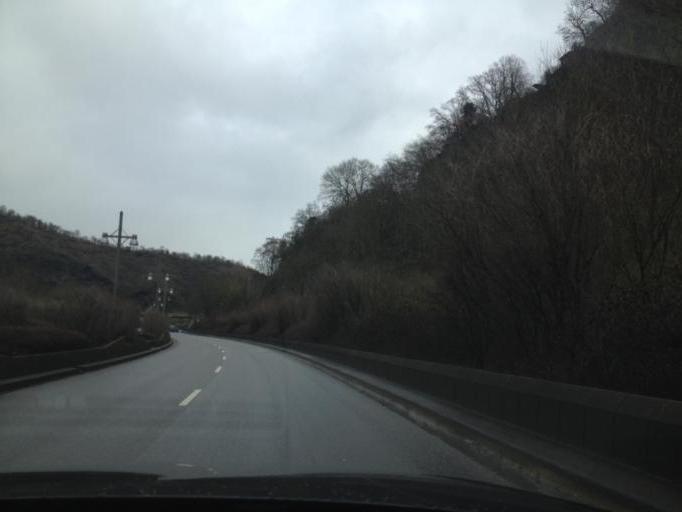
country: DE
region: Rheinland-Pfalz
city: Hintertiefenbach
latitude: 49.7024
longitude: 7.3388
